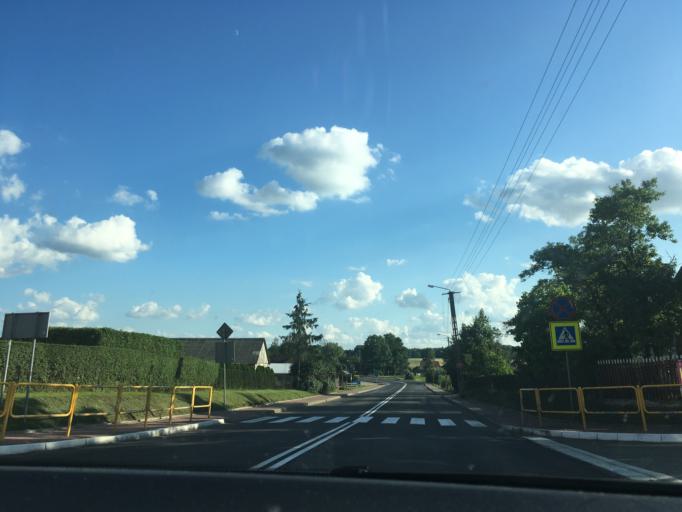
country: PL
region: Podlasie
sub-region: Powiat siemiatycki
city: Dziadkowice
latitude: 52.5650
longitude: 22.9123
